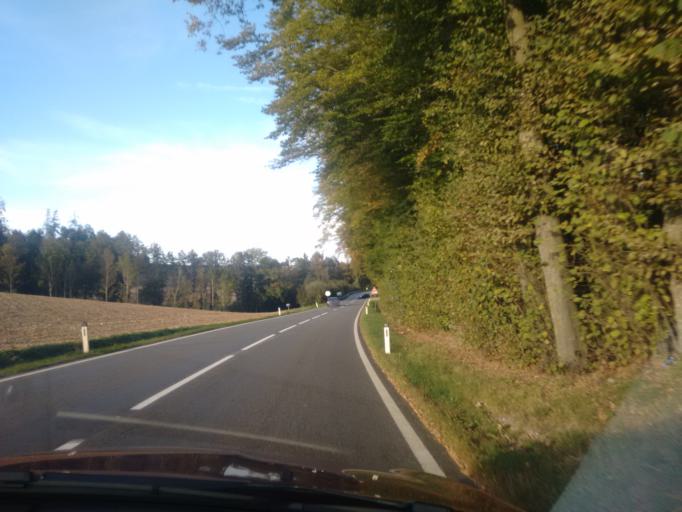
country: AT
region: Upper Austria
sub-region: Politischer Bezirk Vocklabruck
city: Niederthalheim
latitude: 48.1547
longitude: 13.7350
